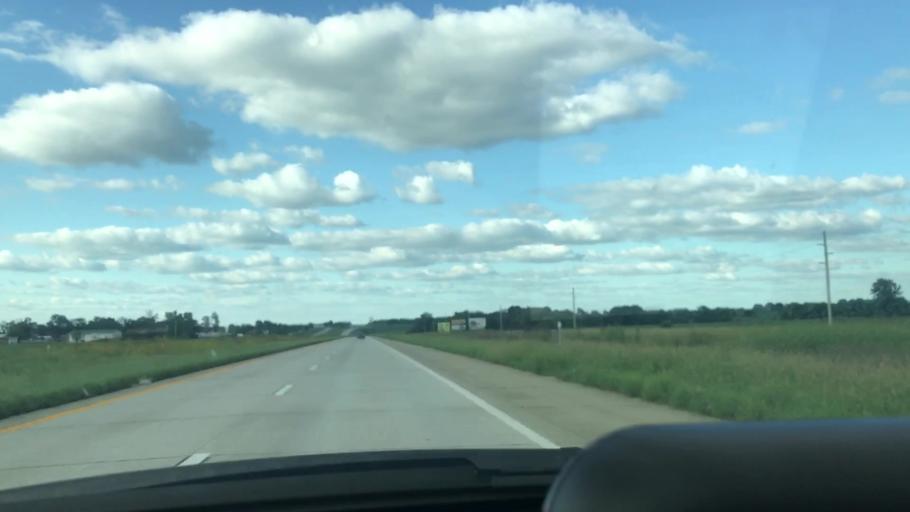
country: US
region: Missouri
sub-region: Benton County
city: Cole Camp
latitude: 38.5173
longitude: -93.2724
